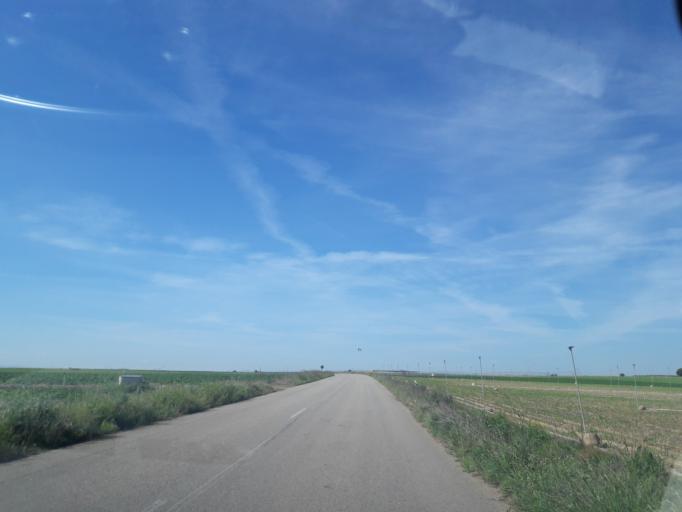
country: ES
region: Castille and Leon
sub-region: Provincia de Salamanca
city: Villoruela
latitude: 41.0343
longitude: -5.3898
